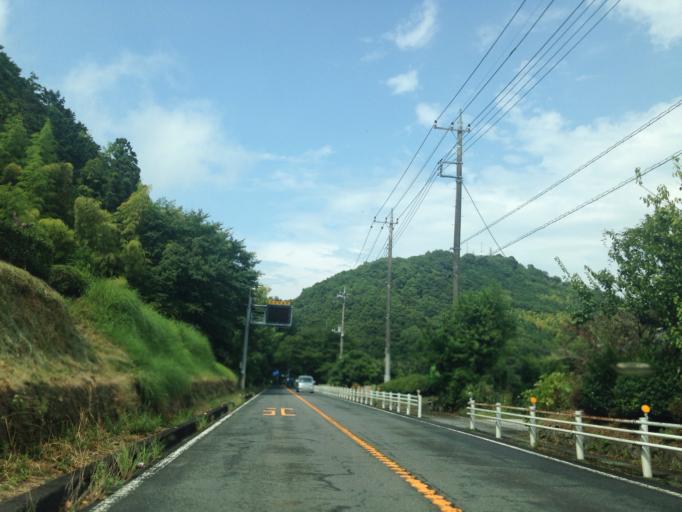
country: JP
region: Shizuoka
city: Ito
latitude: 34.9678
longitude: 138.9393
